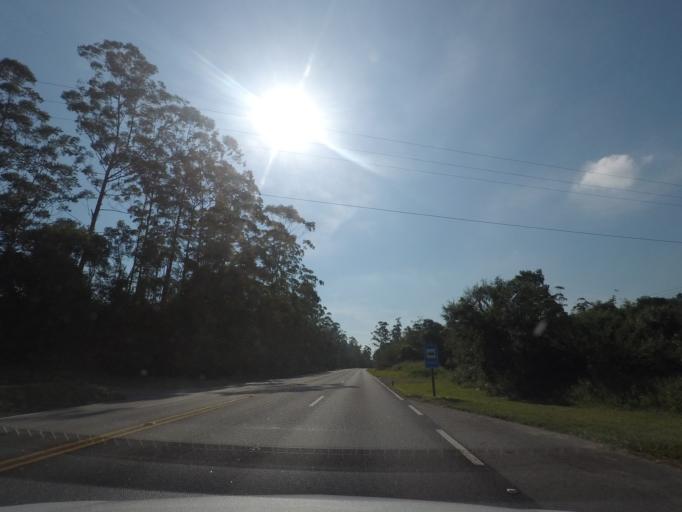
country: BR
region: Parana
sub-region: Pontal Do Parana
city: Pontal do Parana
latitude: -25.6041
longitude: -48.6082
